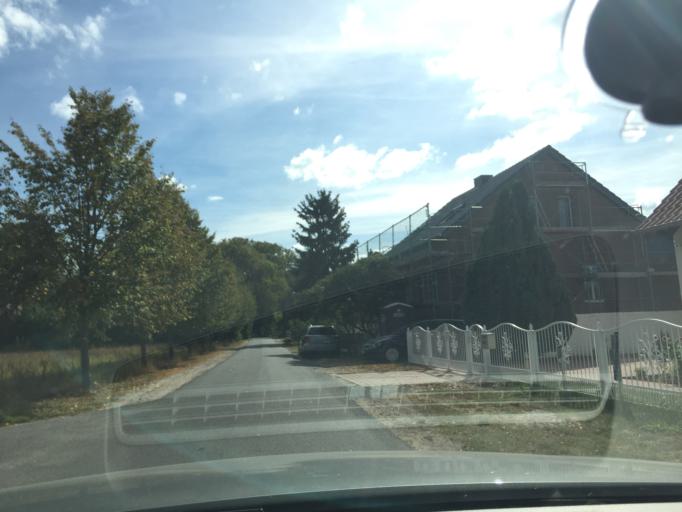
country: DE
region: Brandenburg
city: Spreenhagen
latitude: 52.3873
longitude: 13.8906
